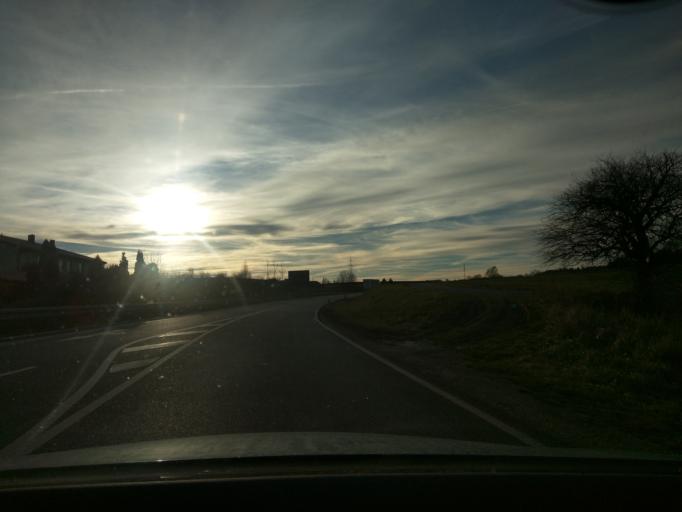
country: DE
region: Bavaria
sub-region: Upper Bavaria
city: Au in der Hallertau
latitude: 48.5661
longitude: 11.7401
